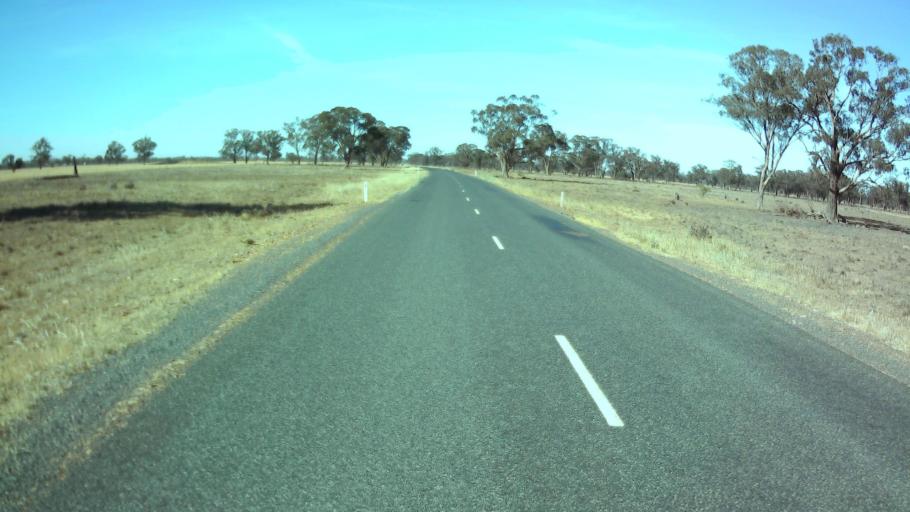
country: AU
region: New South Wales
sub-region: Weddin
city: Grenfell
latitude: -34.0778
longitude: 147.8983
